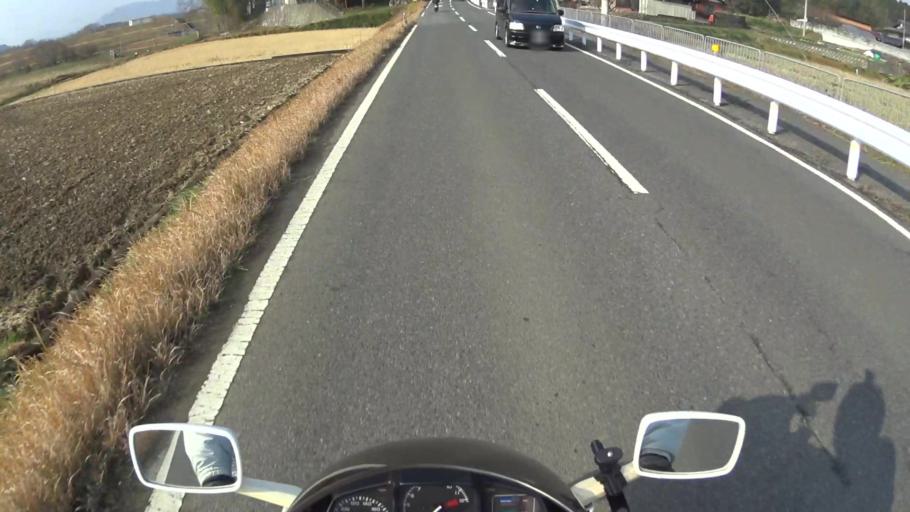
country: JP
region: Kyoto
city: Fukuchiyama
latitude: 35.3141
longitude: 135.1260
